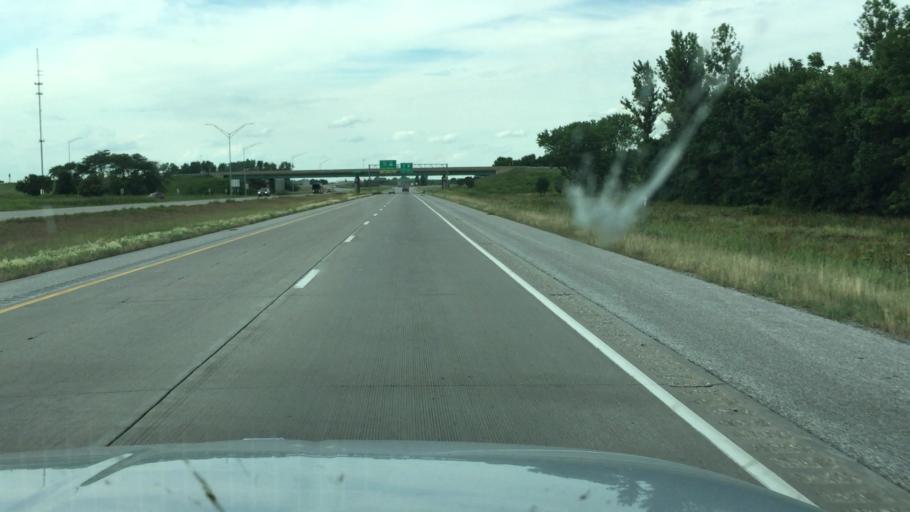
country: US
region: Iowa
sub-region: Scott County
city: Walcott
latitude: 41.5891
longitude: -90.6757
